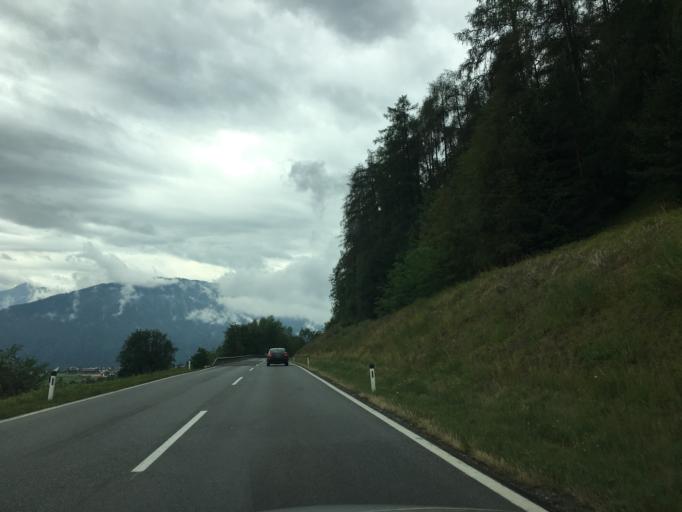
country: AT
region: Tyrol
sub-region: Politischer Bezirk Imst
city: Tarrenz
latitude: 47.2589
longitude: 10.7545
